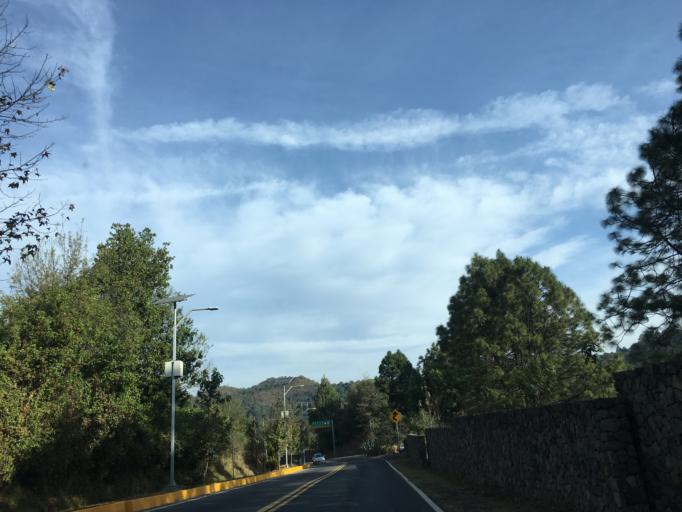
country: MX
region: Mexico
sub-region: Valle de Bravo
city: Colonia Rincon Villa del Valle
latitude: 19.1999
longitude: -100.1000
